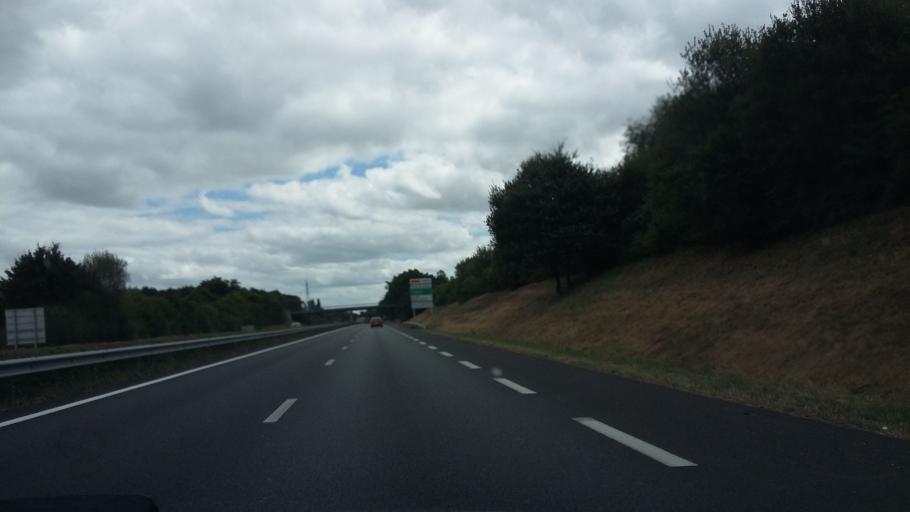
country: FR
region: Pays de la Loire
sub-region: Departement de la Vendee
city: Challans
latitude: 46.8596
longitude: -1.8567
